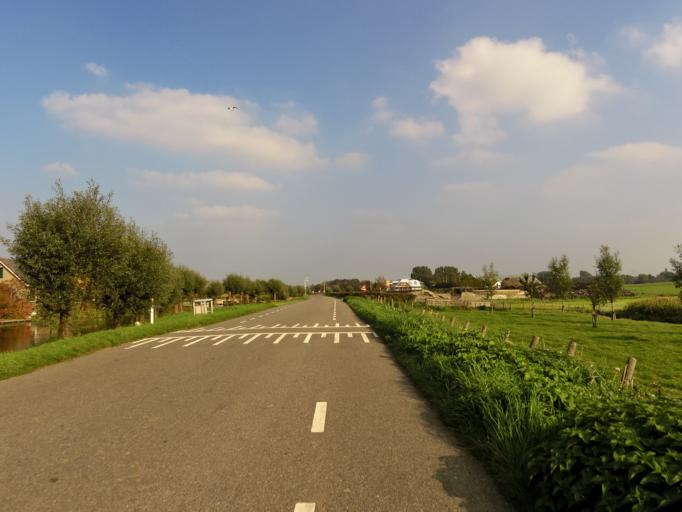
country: NL
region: South Holland
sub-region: Gemeente Rijnwoude
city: Benthuizen
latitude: 52.1043
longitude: 4.5452
